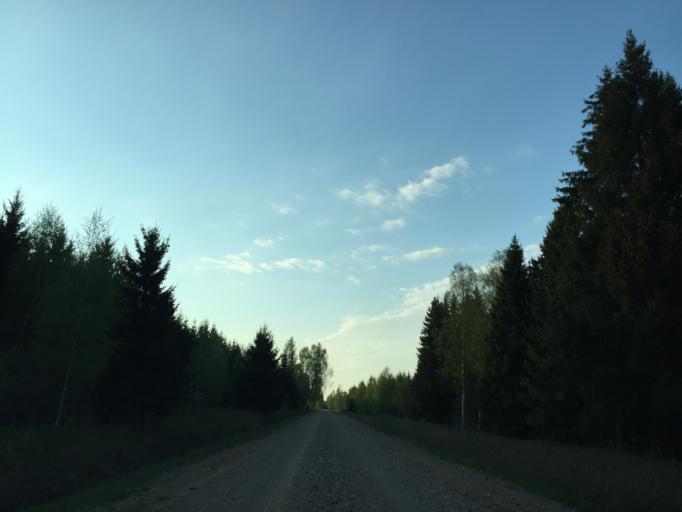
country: LV
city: Tireli
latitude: 56.8494
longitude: 23.6949
